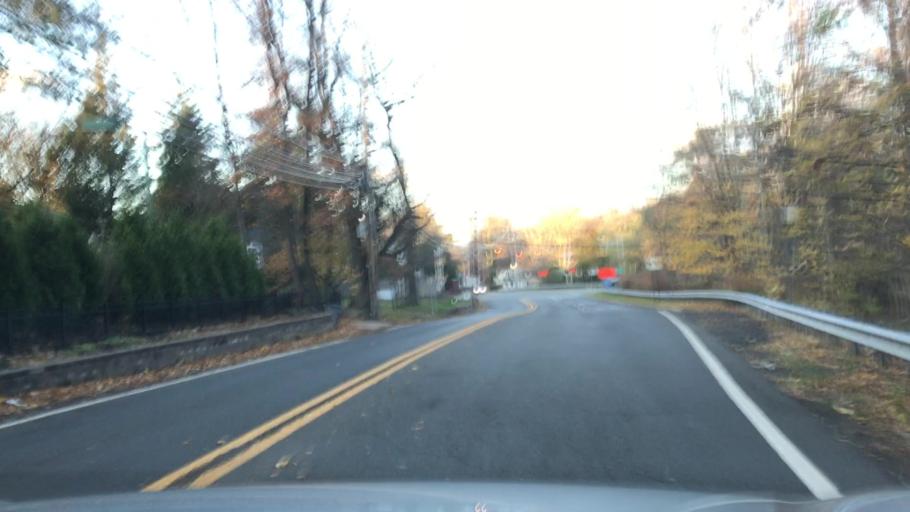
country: US
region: New Jersey
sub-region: Bergen County
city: Harrington Park
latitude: 40.9864
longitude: -73.9752
